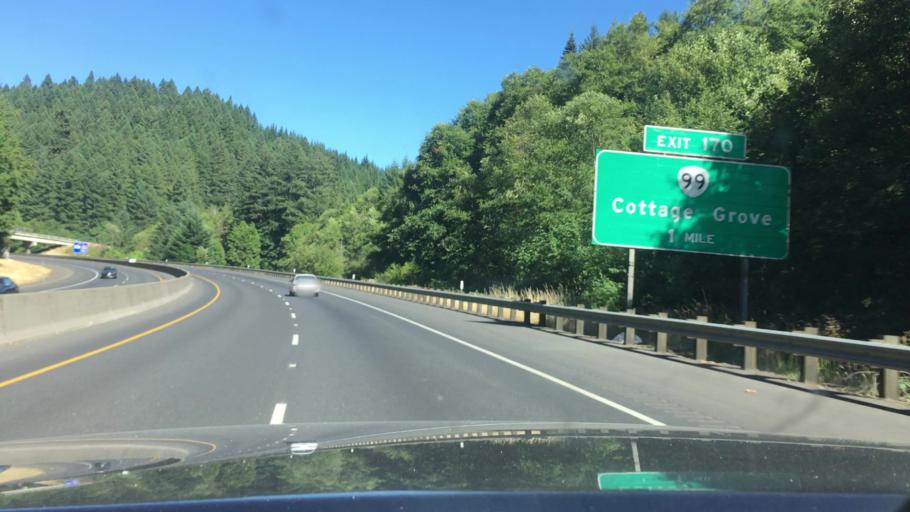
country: US
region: Oregon
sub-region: Lane County
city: Cottage Grove
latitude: 43.7517
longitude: -123.1491
